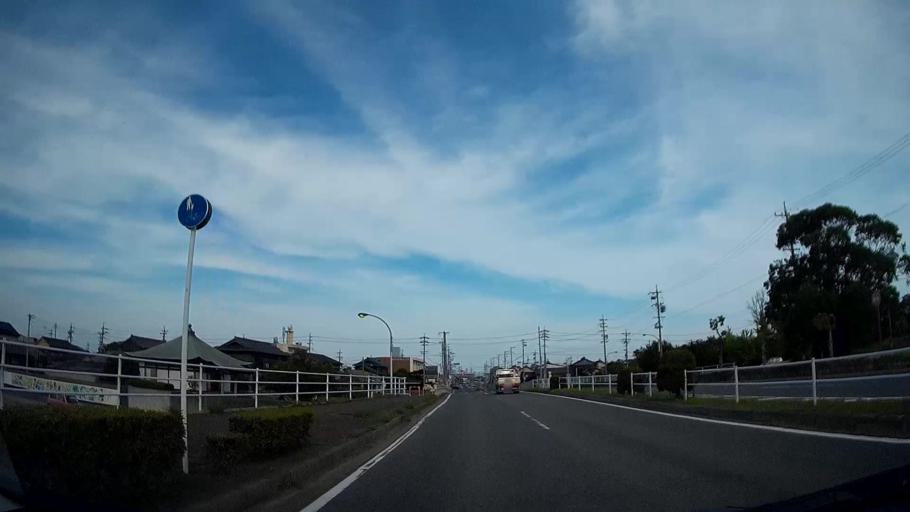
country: JP
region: Aichi
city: Hekinan
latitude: 34.8695
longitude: 136.9761
